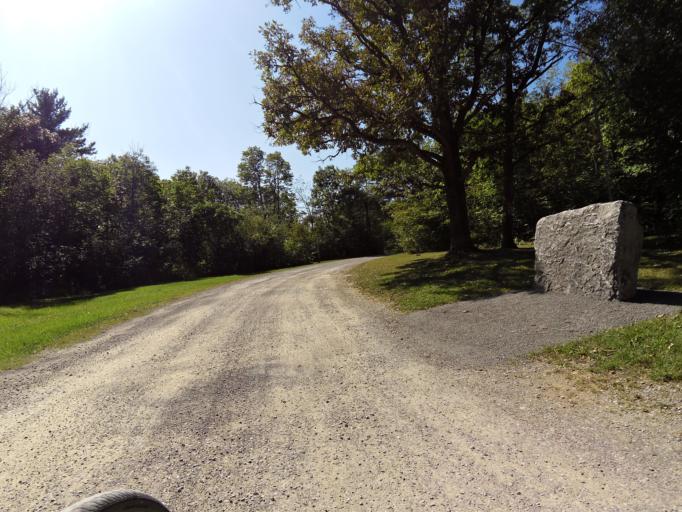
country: CA
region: Ontario
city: Bells Corners
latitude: 45.4066
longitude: -75.9271
